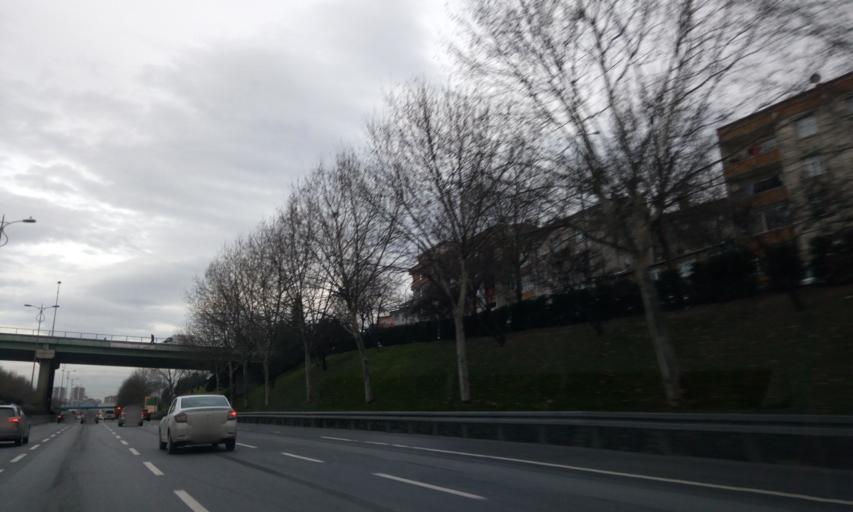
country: TR
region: Istanbul
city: Bagcilar
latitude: 41.0544
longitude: 28.8600
